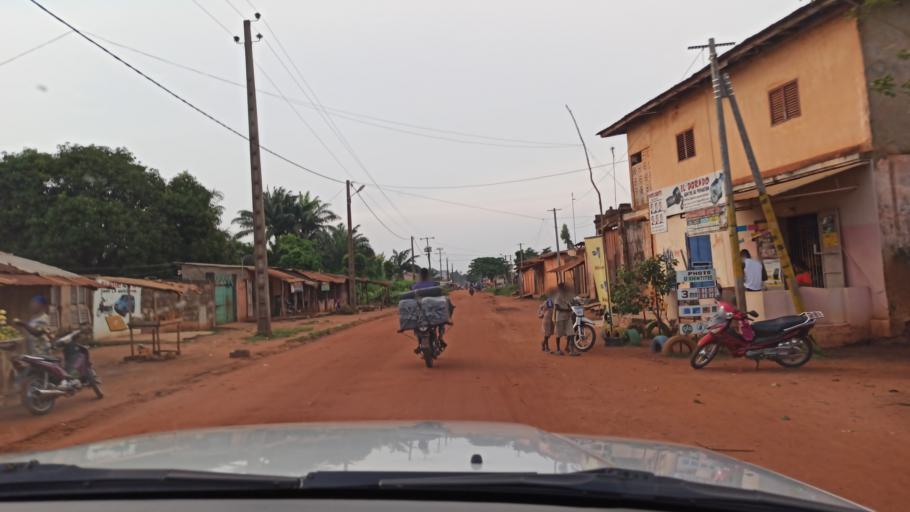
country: BJ
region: Queme
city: Porto-Novo
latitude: 6.5266
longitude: 2.6695
